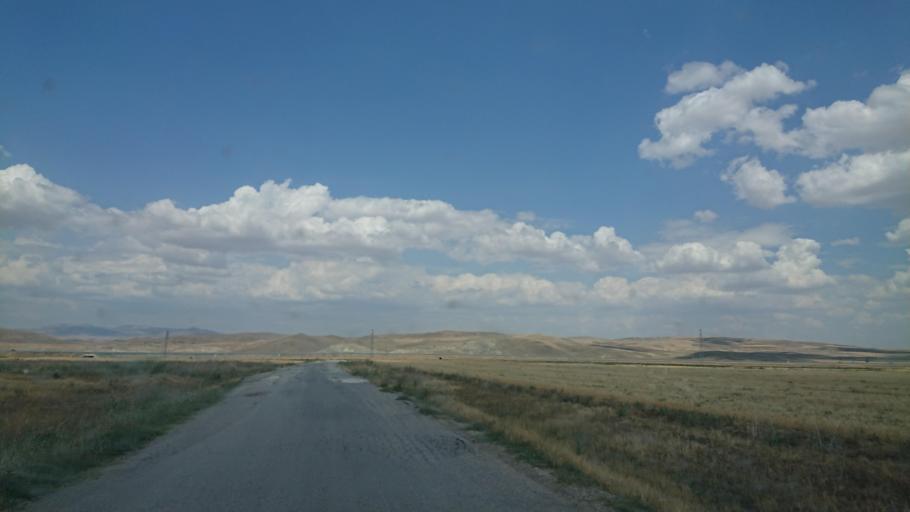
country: TR
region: Aksaray
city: Sariyahsi
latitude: 38.9689
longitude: 33.8968
